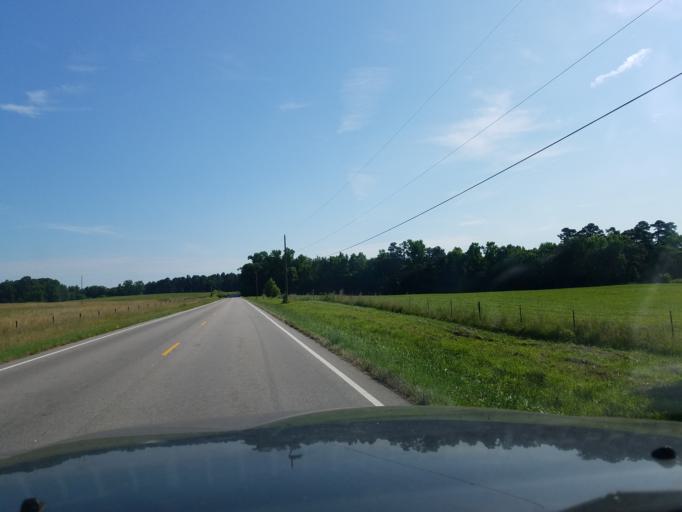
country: US
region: North Carolina
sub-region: Granville County
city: Butner
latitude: 36.1679
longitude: -78.7598
